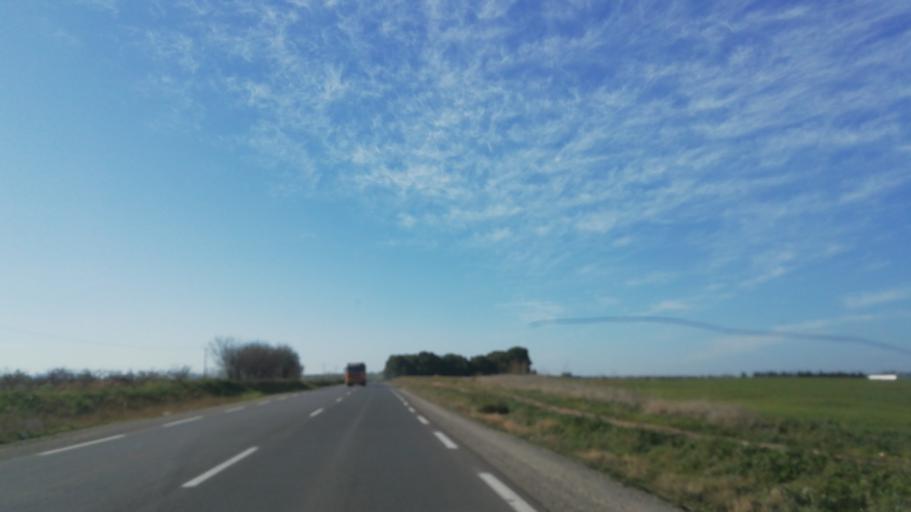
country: DZ
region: Tlemcen
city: Ouled Mimoun
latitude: 35.0327
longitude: -0.8637
